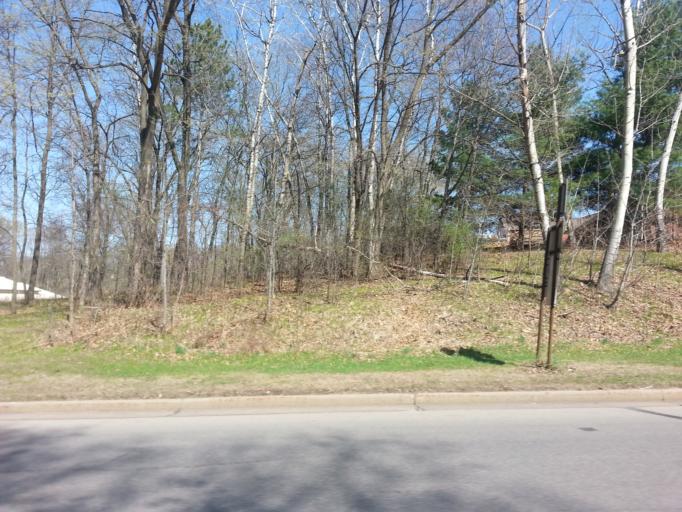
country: US
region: Wisconsin
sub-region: Dunn County
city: Menomonie
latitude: 44.8590
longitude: -91.9297
